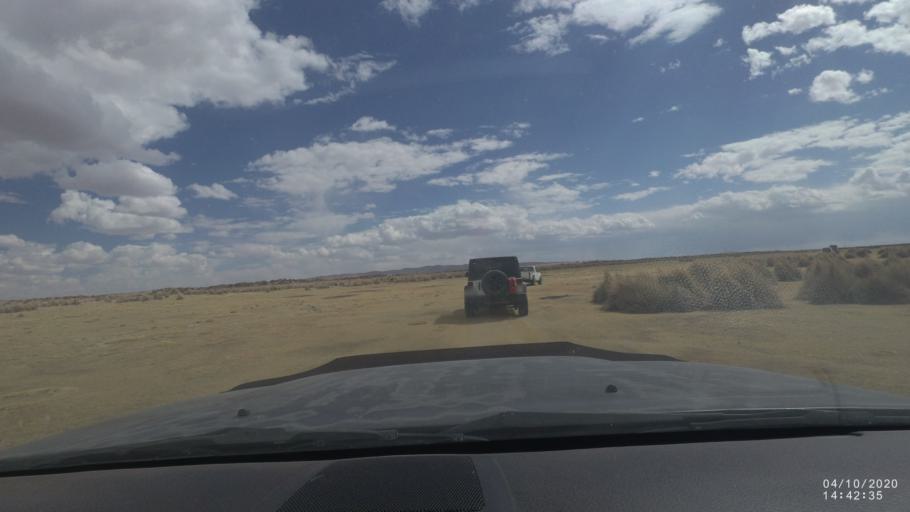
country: BO
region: Oruro
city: Poopo
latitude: -18.6867
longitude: -67.4914
